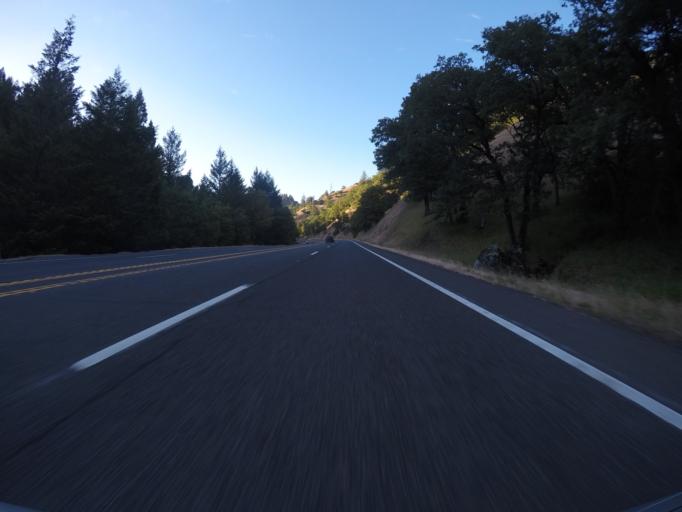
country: US
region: California
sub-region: Mendocino County
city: Laytonville
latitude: 39.6118
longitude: -123.4589
